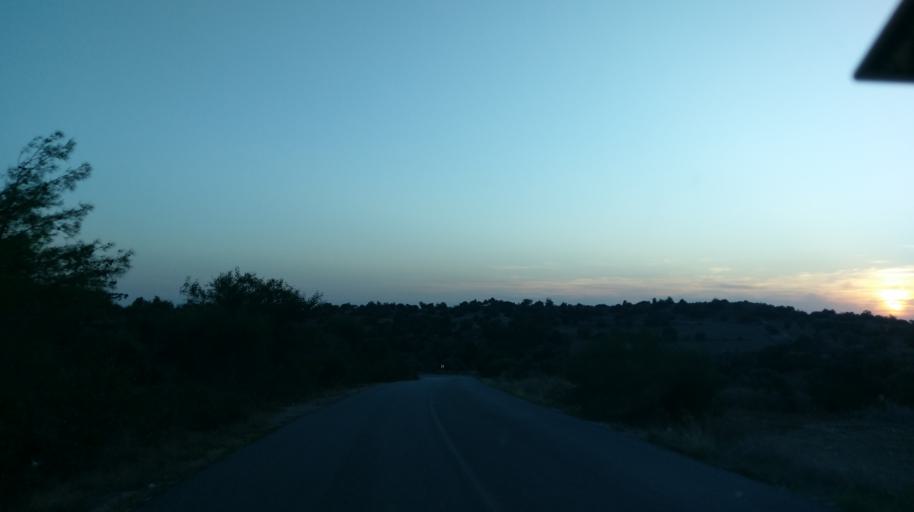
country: CY
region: Ammochostos
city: Trikomo
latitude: 35.3193
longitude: 33.8793
